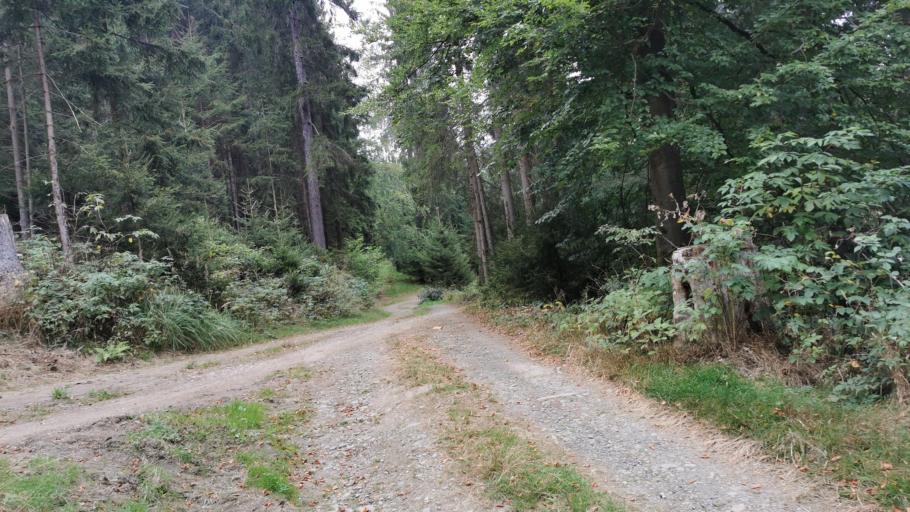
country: DE
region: Bavaria
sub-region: Upper Franconia
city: Steinwiesen
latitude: 50.3425
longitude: 11.4526
